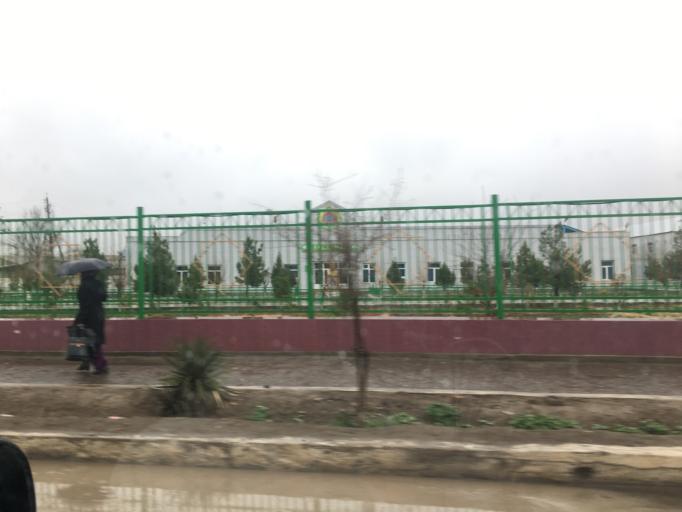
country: TM
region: Mary
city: Yoloeten
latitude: 37.2914
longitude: 62.3575
